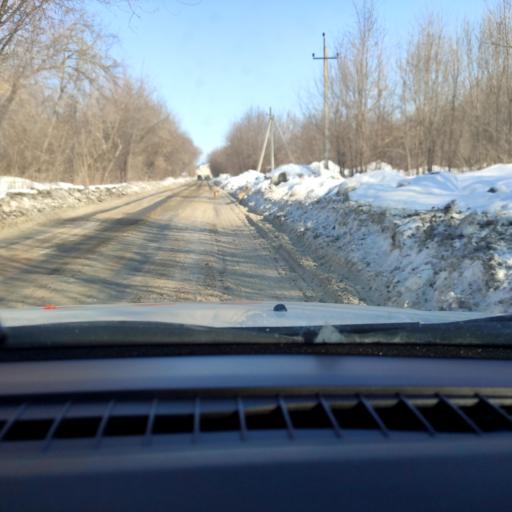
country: RU
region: Samara
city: Novokuybyshevsk
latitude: 53.1173
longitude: 49.9070
